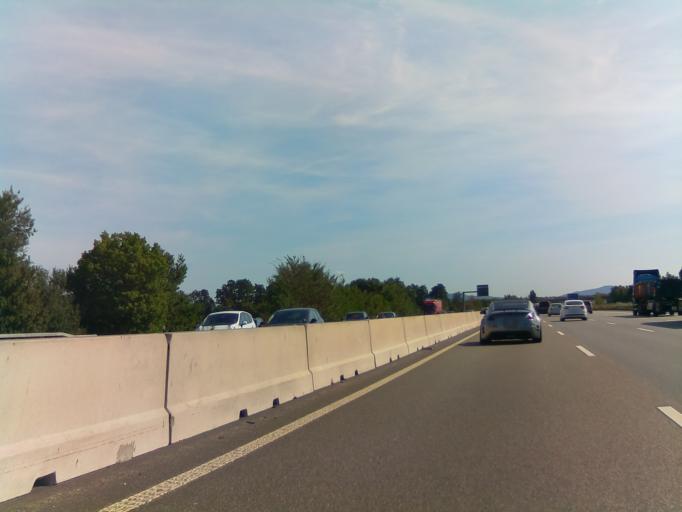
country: DE
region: Hesse
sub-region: Regierungsbezirk Darmstadt
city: Erzhausen
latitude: 49.9383
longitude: 8.6121
